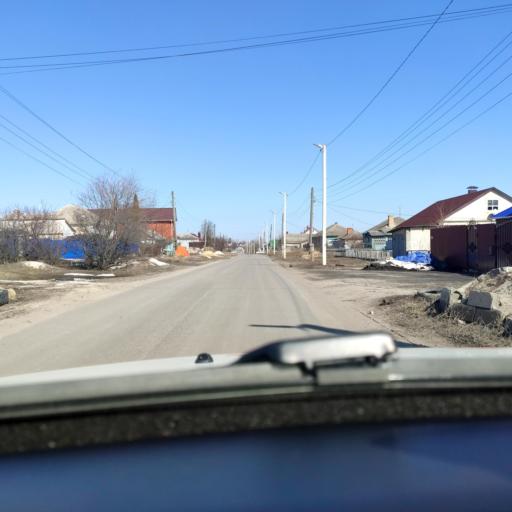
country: RU
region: Voronezj
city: Devitsa
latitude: 51.6368
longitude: 38.9342
